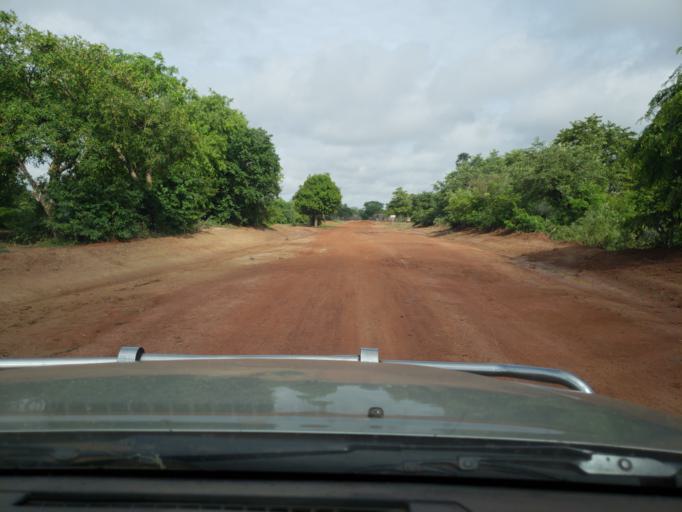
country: ML
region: Sikasso
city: Koutiala
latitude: 12.3925
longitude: -6.0205
